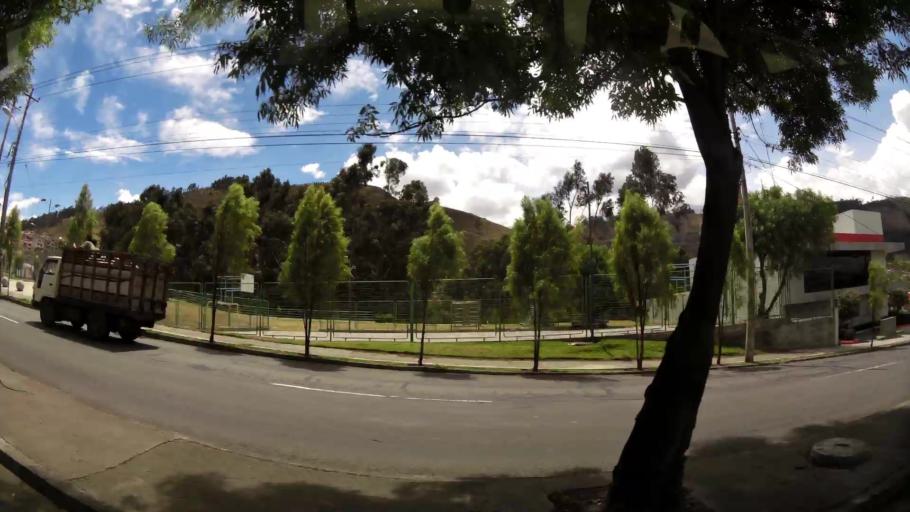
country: EC
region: Tungurahua
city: Ambato
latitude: -1.2577
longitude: -78.6411
